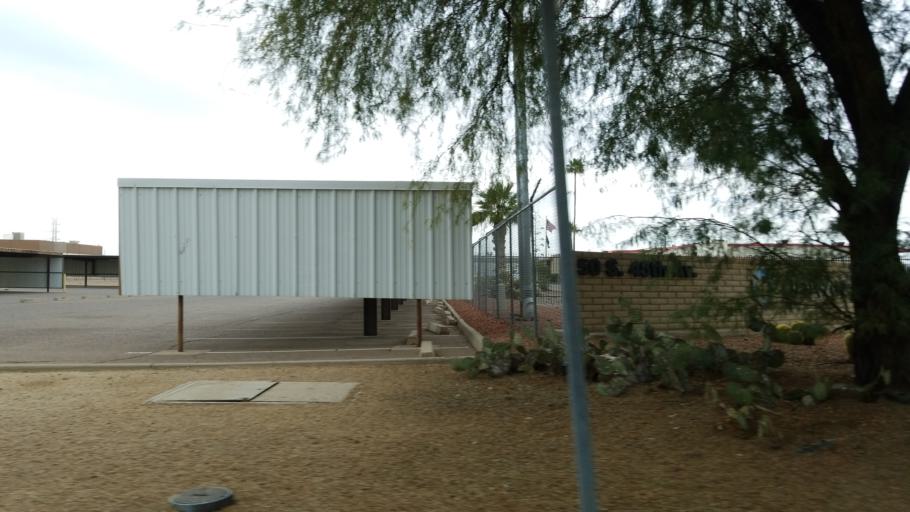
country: US
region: Arizona
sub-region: Maricopa County
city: Phoenix
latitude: 33.4465
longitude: -112.1561
